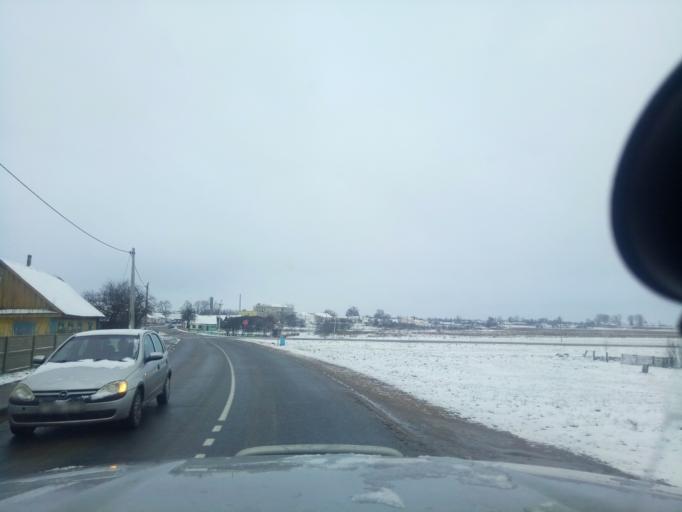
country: BY
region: Minsk
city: Tsimkavichy
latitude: 53.0687
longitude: 26.9890
